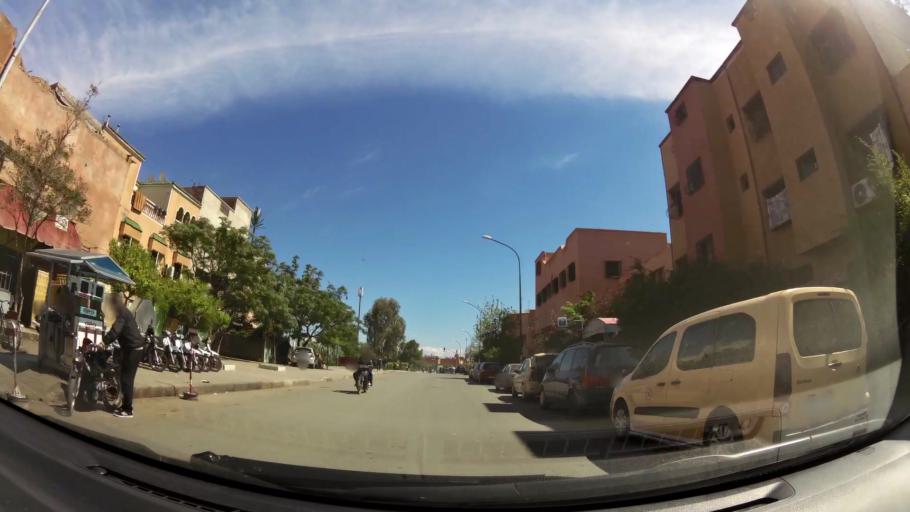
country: MA
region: Marrakech-Tensift-Al Haouz
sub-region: Marrakech
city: Marrakesh
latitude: 31.6044
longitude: -7.9624
